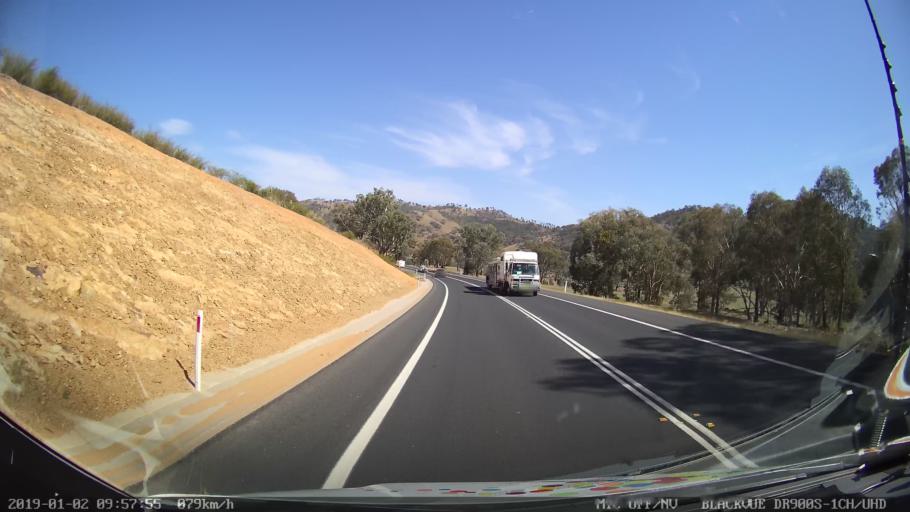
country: AU
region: New South Wales
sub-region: Tumut Shire
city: Tumut
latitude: -35.1999
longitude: 148.1643
